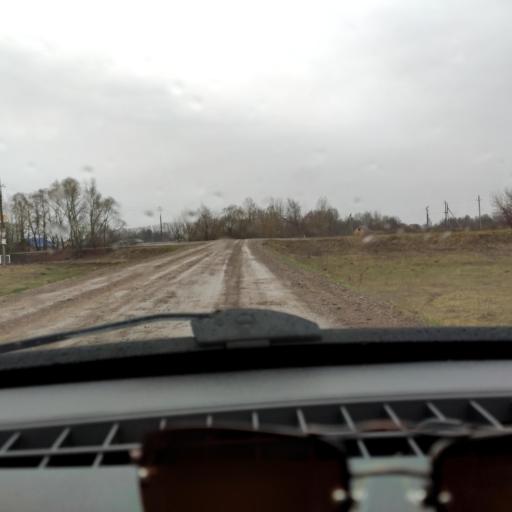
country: RU
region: Bashkortostan
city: Kabakovo
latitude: 54.5627
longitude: 56.0491
